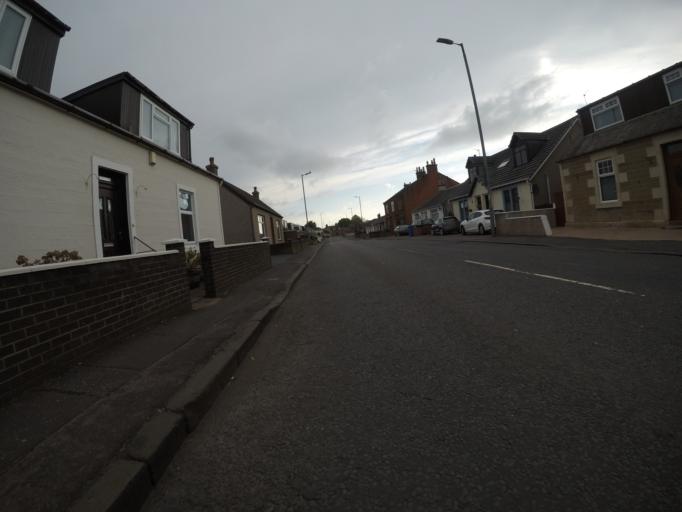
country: GB
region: Scotland
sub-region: North Ayrshire
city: Dreghorn
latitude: 55.6081
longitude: -4.6209
